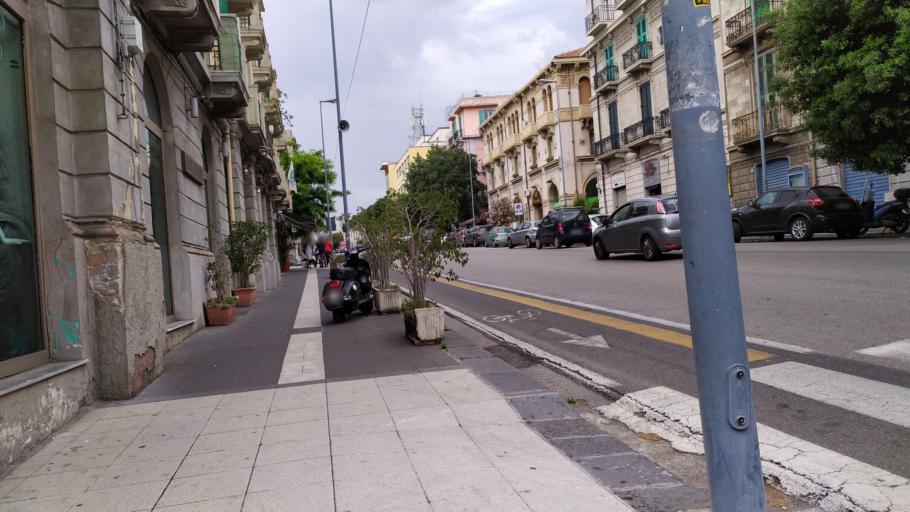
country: IT
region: Sicily
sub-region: Messina
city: Messina
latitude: 38.1914
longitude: 15.5529
